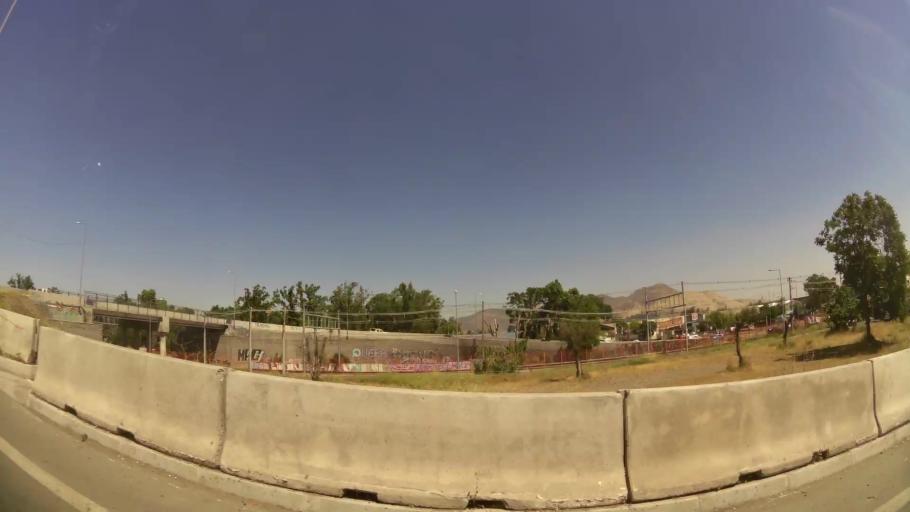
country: CL
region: Santiago Metropolitan
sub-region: Provincia de Maipo
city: San Bernardo
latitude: -33.6204
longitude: -70.6986
